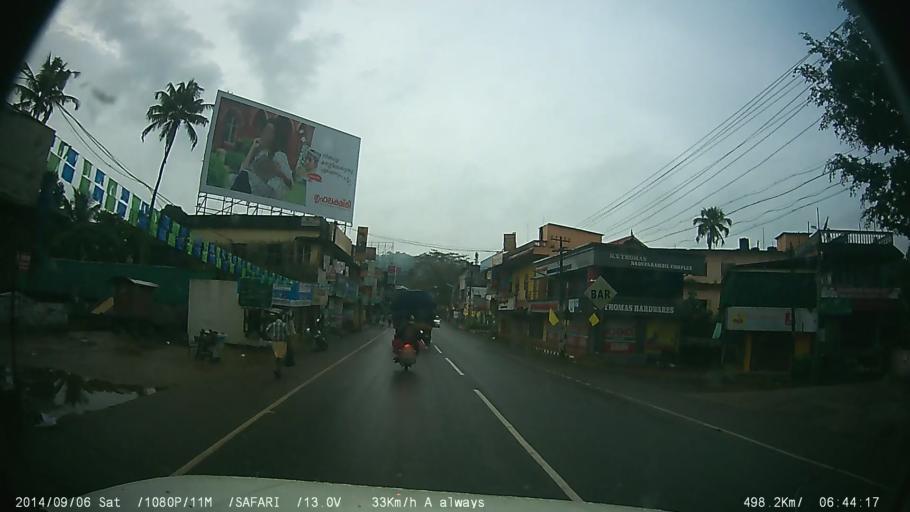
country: IN
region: Kerala
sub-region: Kottayam
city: Vaikam
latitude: 9.7678
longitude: 76.4907
